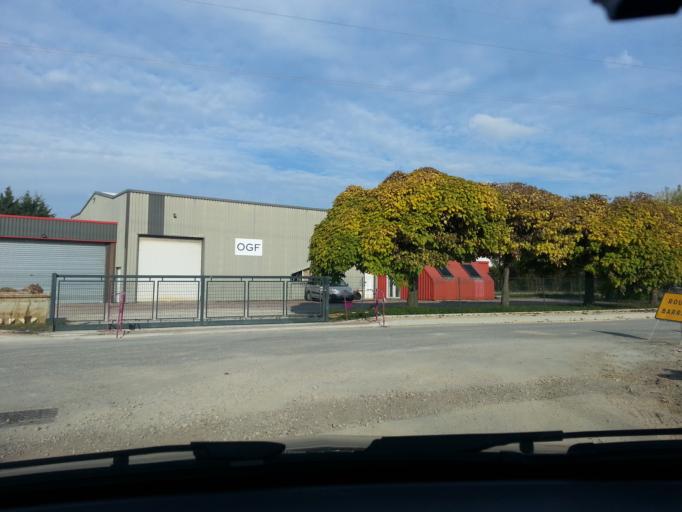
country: FR
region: Bourgogne
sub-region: Departement de Saone-et-Loire
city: Chatenoy-le-Royal
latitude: 46.7963
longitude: 4.7907
